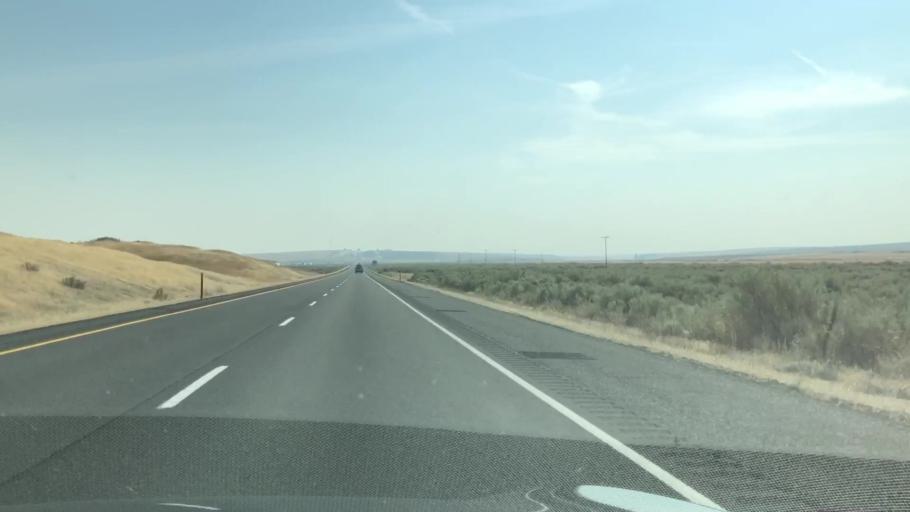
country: US
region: Washington
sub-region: Grant County
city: Warden
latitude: 47.0870
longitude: -118.9109
